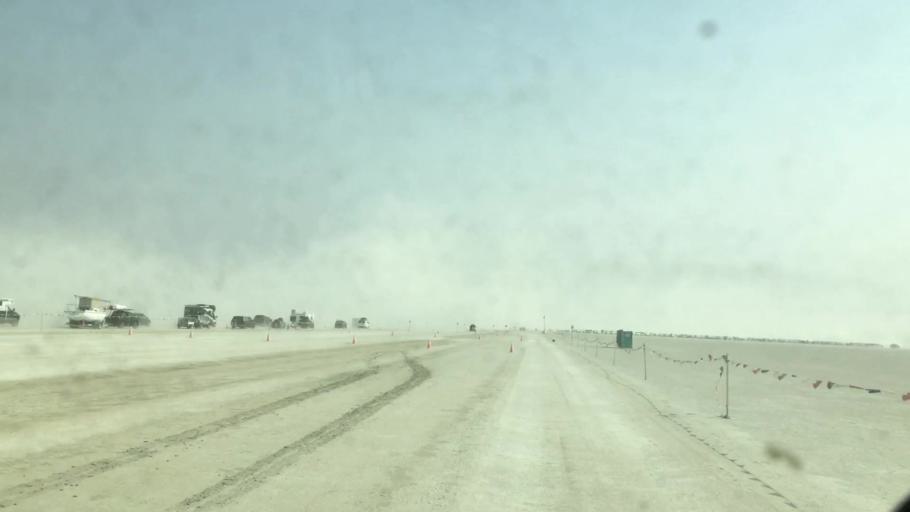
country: US
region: Nevada
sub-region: Pershing County
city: Lovelock
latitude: 40.7587
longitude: -119.2535
